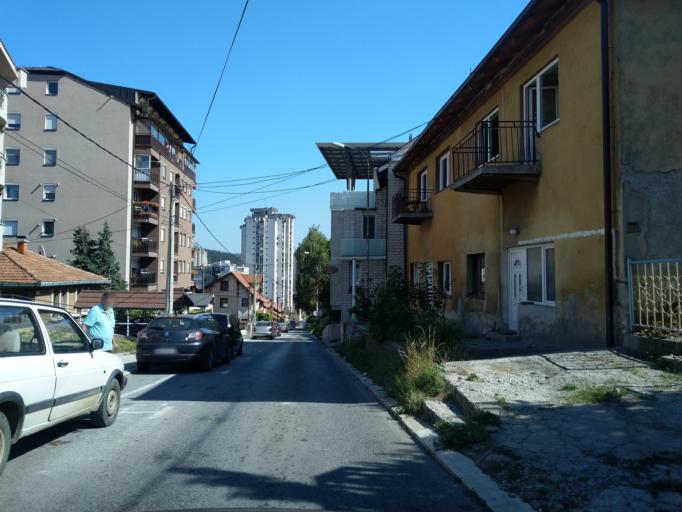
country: RS
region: Central Serbia
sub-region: Zlatiborski Okrug
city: Uzice
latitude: 43.8568
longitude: 19.8313
